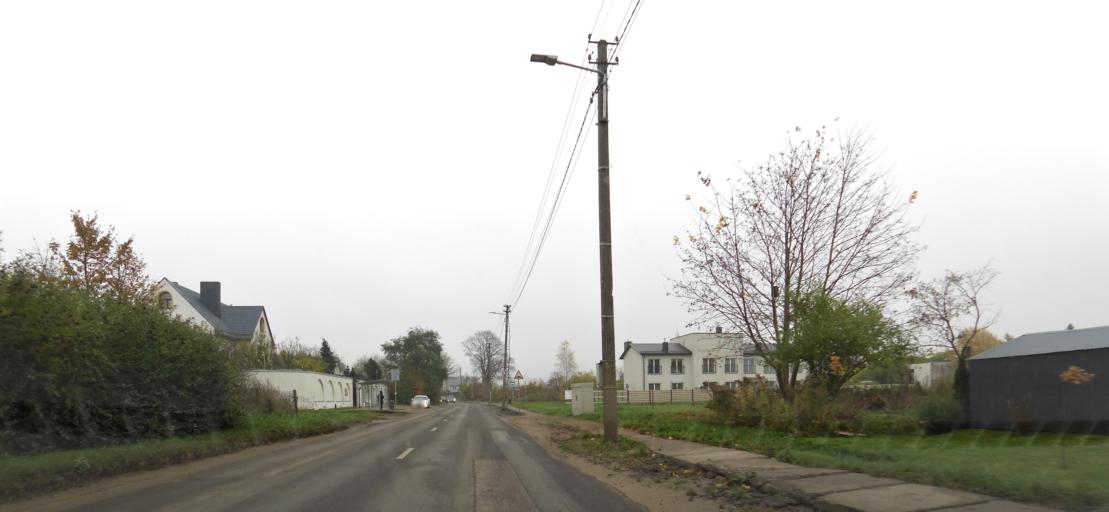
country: LT
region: Vilnius County
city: Rasos
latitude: 54.6605
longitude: 25.3544
